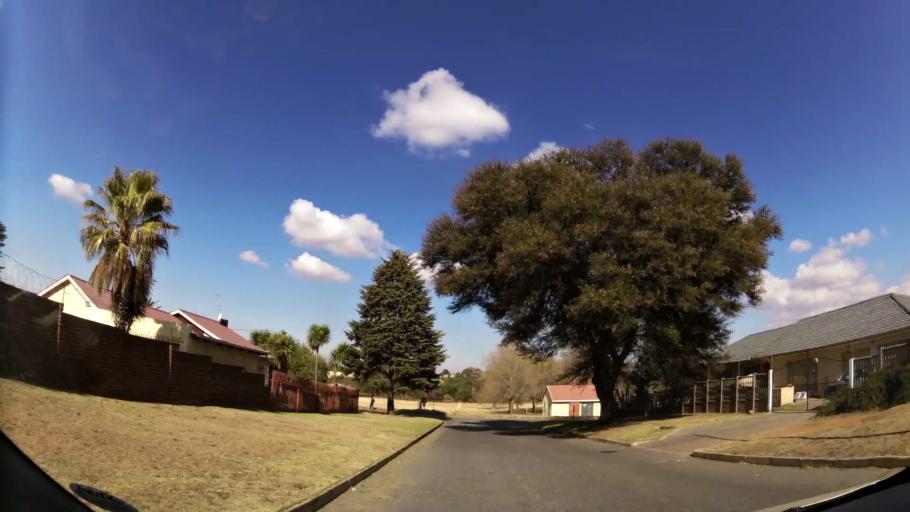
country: ZA
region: Gauteng
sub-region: City of Johannesburg Metropolitan Municipality
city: Roodepoort
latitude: -26.1253
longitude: 27.8241
